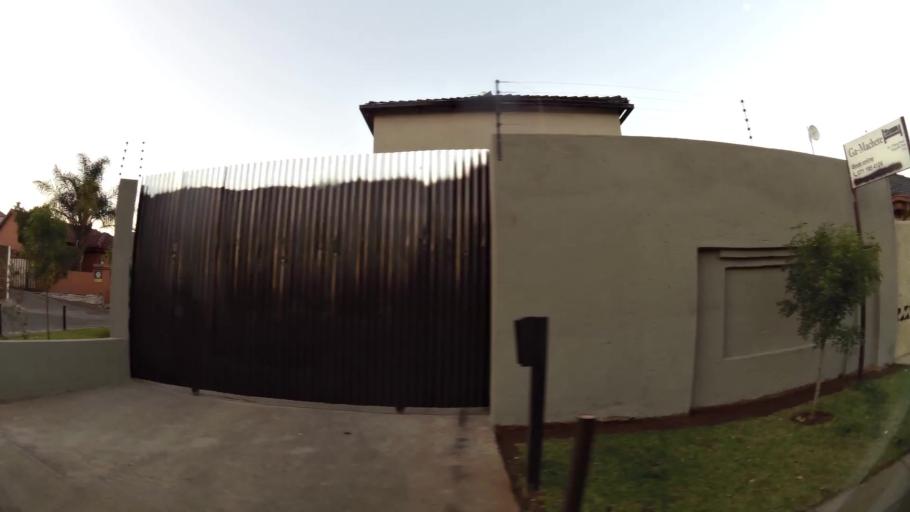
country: ZA
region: Gauteng
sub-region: City of Tshwane Metropolitan Municipality
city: Pretoria
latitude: -25.7393
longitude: 28.1479
